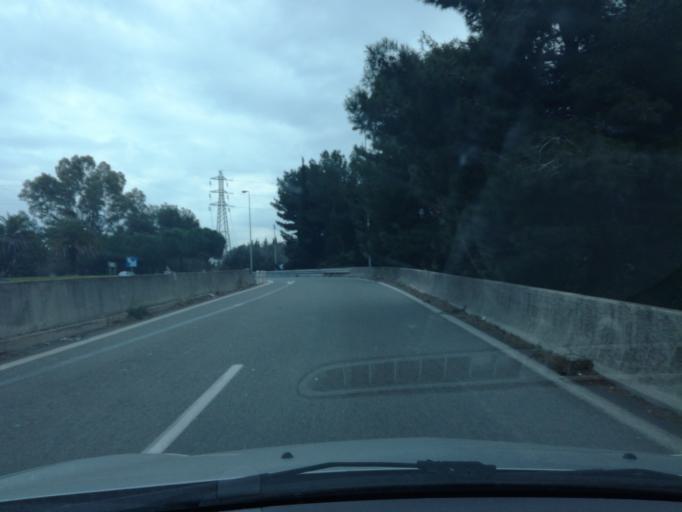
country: FR
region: Provence-Alpes-Cote d'Azur
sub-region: Departement des Alpes-Maritimes
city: Mougins
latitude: 43.5850
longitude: 7.0036
